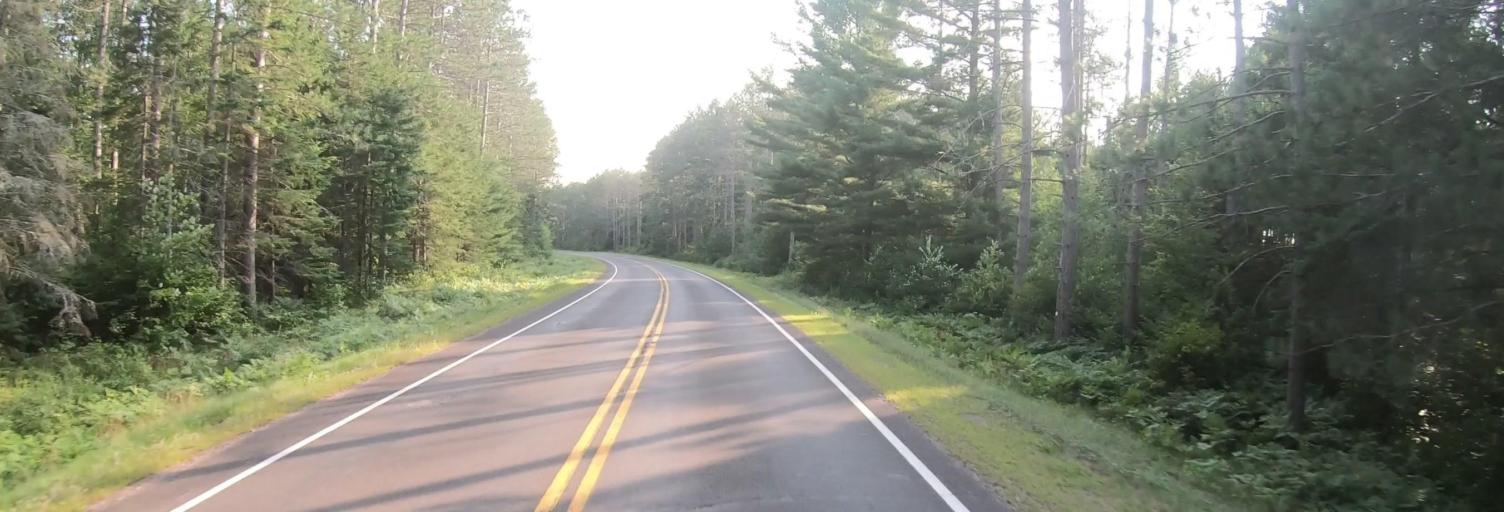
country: US
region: Wisconsin
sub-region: Ashland County
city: Ashland
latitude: 46.1793
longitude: -90.9035
